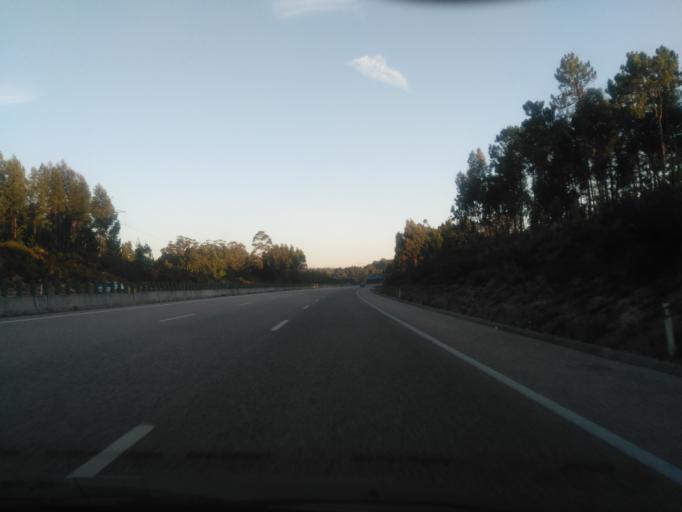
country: PT
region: Leiria
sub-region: Pombal
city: Lourical
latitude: 39.9618
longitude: -8.7757
